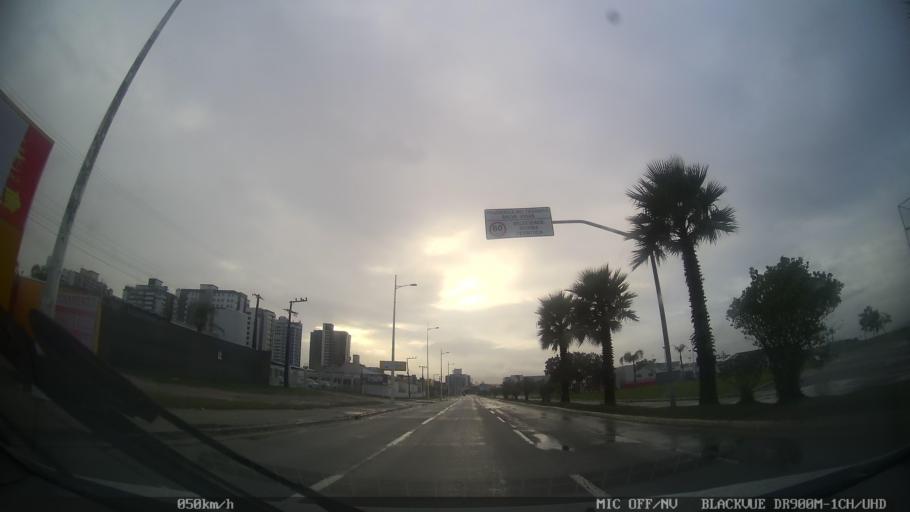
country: BR
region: Santa Catarina
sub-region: Sao Jose
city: Campinas
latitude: -27.6020
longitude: -48.6124
